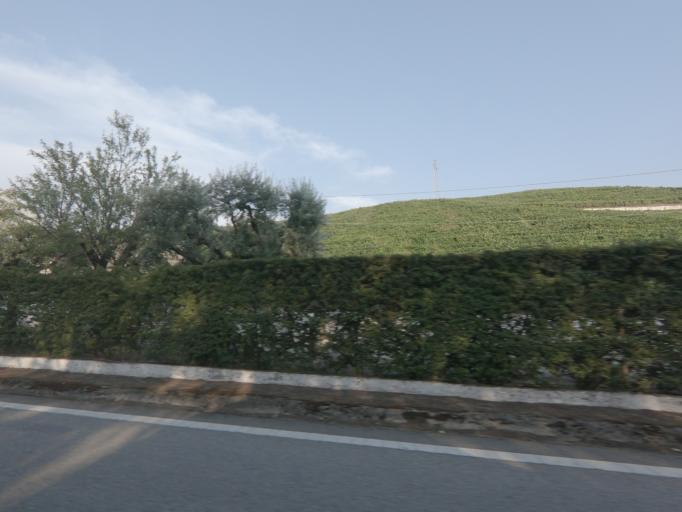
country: PT
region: Viseu
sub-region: Armamar
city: Armamar
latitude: 41.1450
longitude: -7.6885
